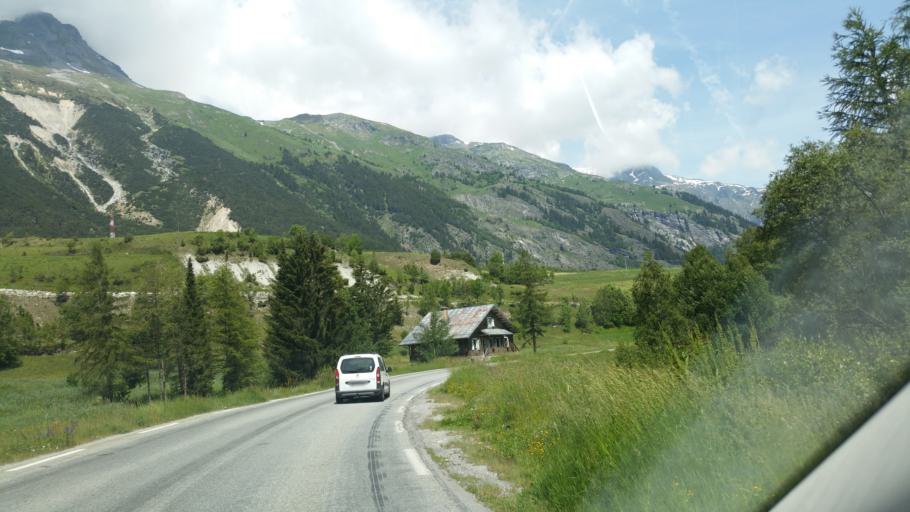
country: FR
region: Rhone-Alpes
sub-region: Departement de la Savoie
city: Modane
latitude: 45.2735
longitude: 6.8134
